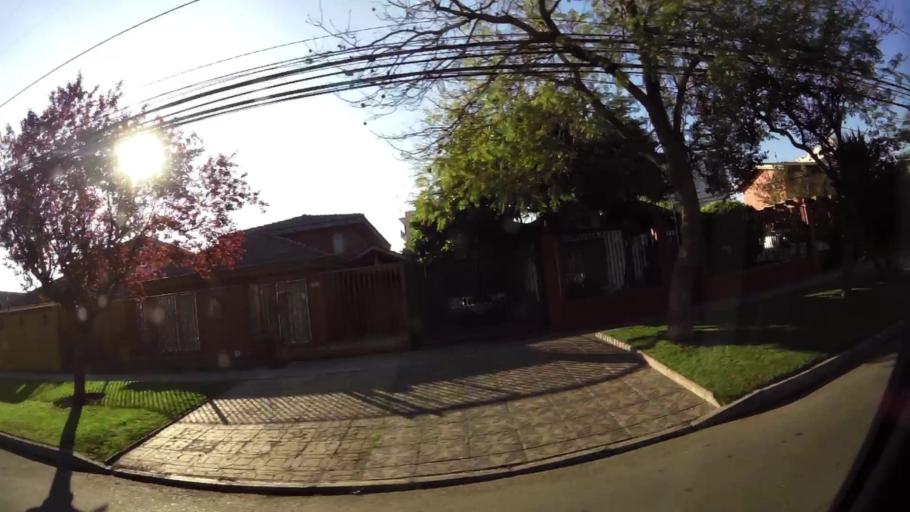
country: CL
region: Santiago Metropolitan
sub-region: Provincia de Santiago
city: Lo Prado
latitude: -33.4845
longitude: -70.7547
